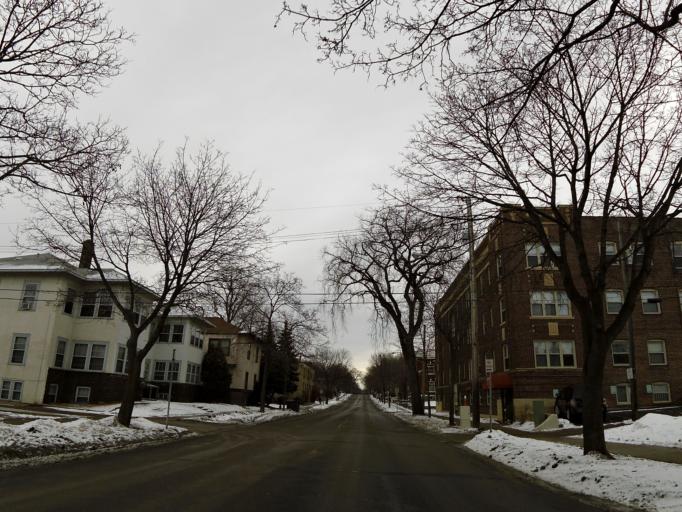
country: US
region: Minnesota
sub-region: Hennepin County
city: Minneapolis
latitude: 44.9591
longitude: -93.2865
